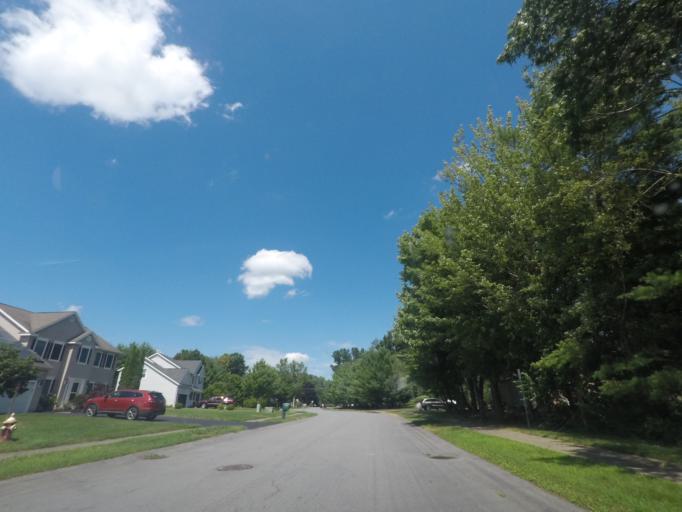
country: US
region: New York
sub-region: Schenectady County
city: Rotterdam
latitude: 42.7453
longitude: -73.9306
